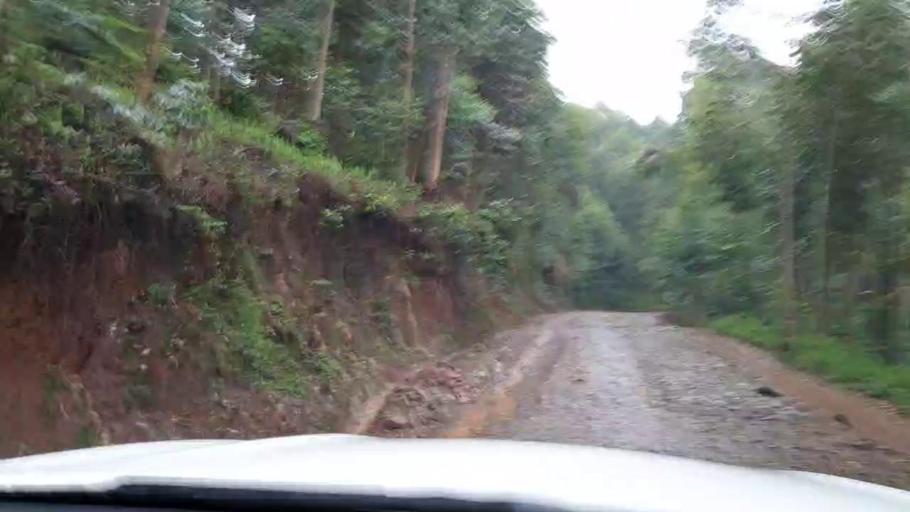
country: RW
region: Western Province
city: Cyangugu
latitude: -2.4716
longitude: 29.0322
